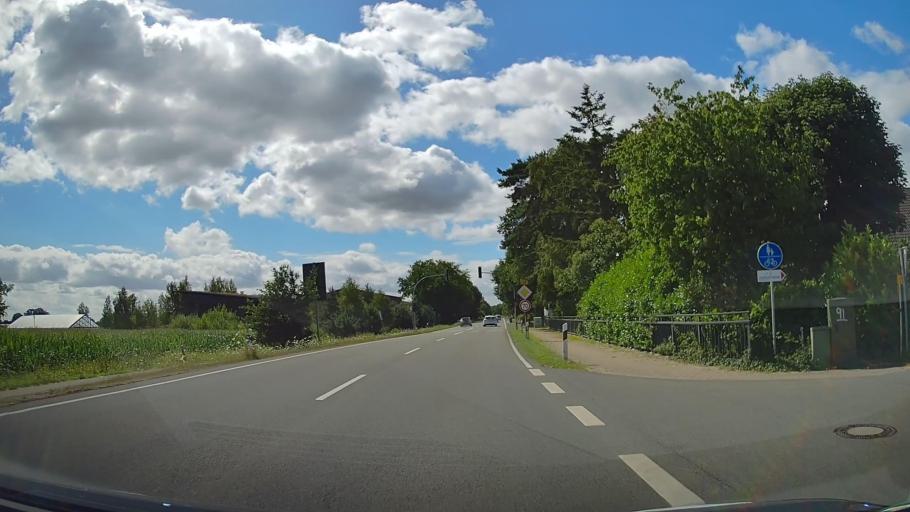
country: DE
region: Lower Saxony
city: Vechta
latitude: 52.6997
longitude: 8.3013
